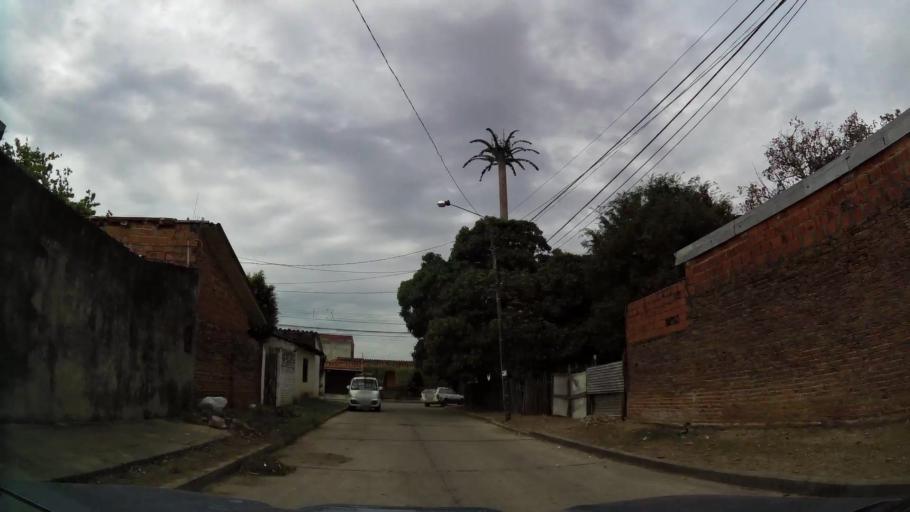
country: BO
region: Santa Cruz
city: Santa Cruz de la Sierra
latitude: -17.7763
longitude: -63.2101
